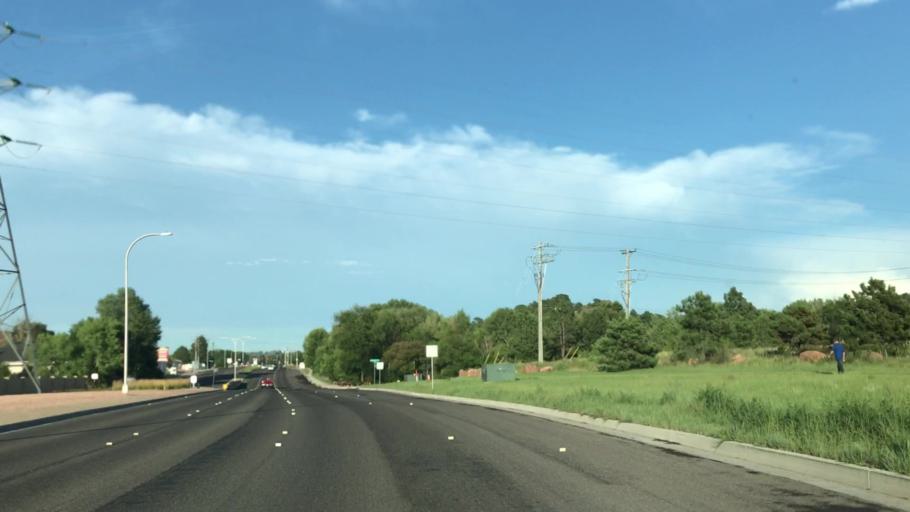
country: US
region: Colorado
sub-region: El Paso County
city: Colorado Springs
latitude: 38.8890
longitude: -104.7751
